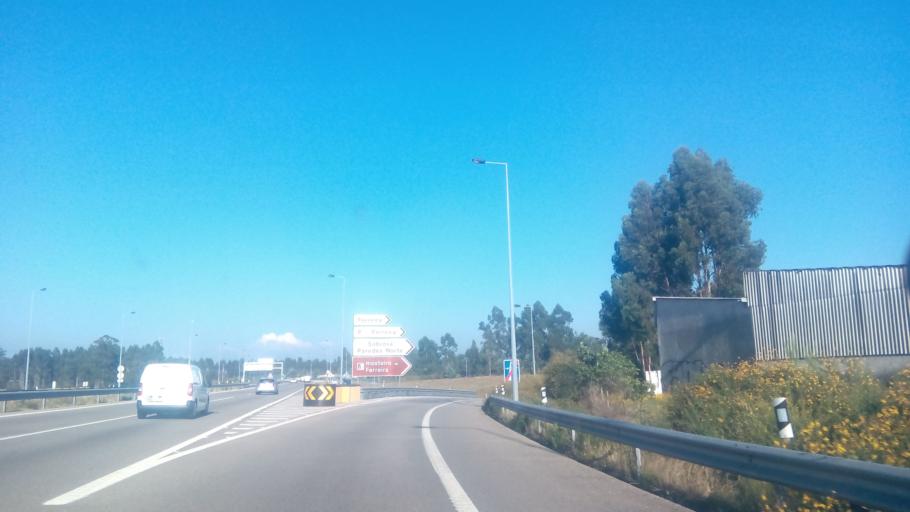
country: PT
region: Porto
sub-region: Pacos de Ferreira
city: Pacos de Ferreira
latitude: 41.2587
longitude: -8.3645
